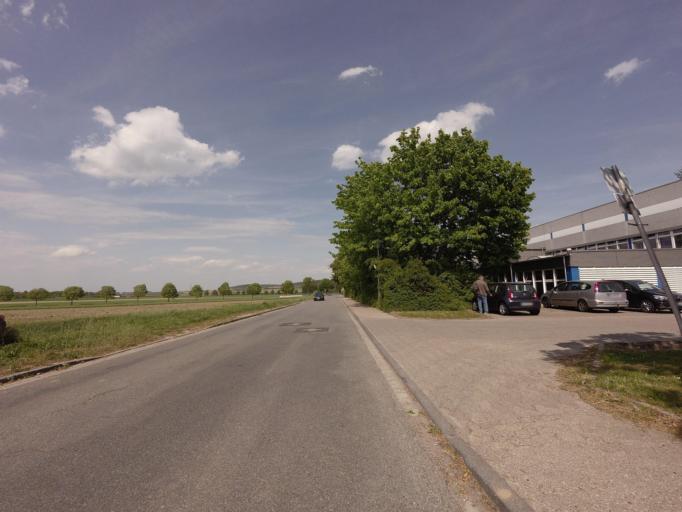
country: DE
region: Lower Saxony
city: Giesen
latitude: 52.1509
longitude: 9.8853
